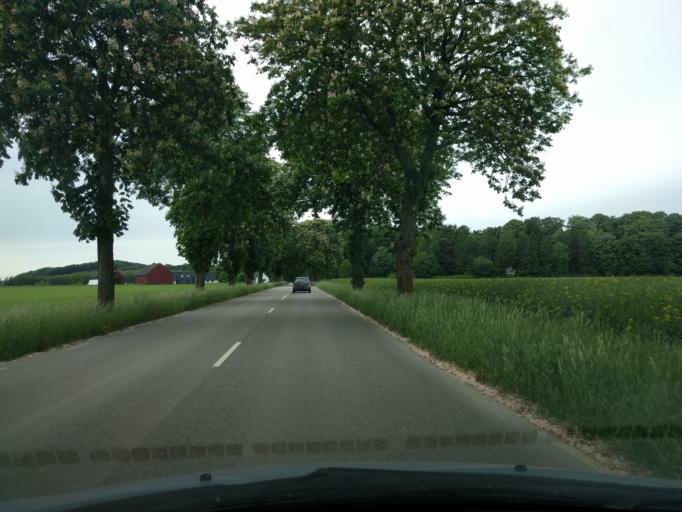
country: SE
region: Skane
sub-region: Malmo
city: Oxie
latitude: 55.5280
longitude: 13.1536
